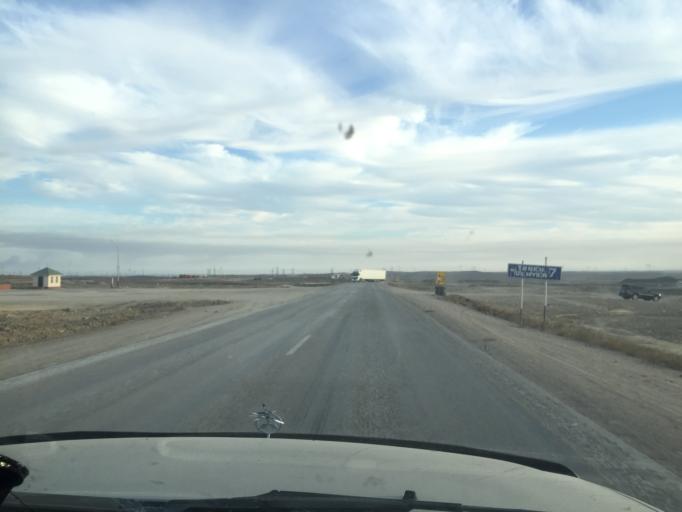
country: KZ
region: Almaty Oblysy
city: Ulken
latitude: 45.1592
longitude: 73.9454
